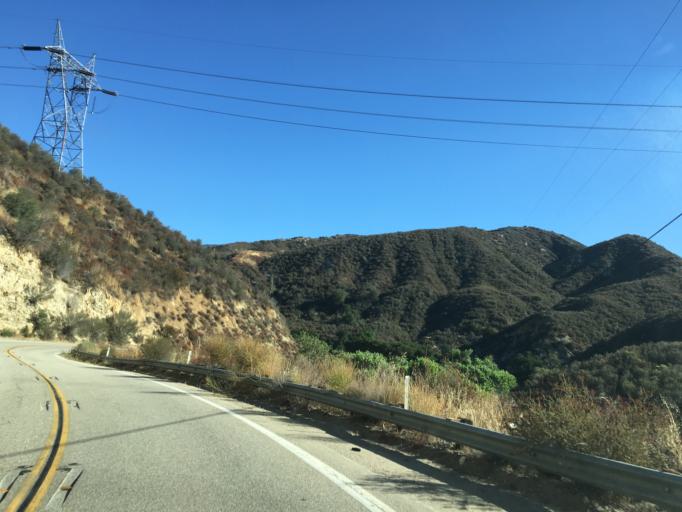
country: US
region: California
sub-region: Los Angeles County
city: Castaic
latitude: 34.6036
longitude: -118.5571
